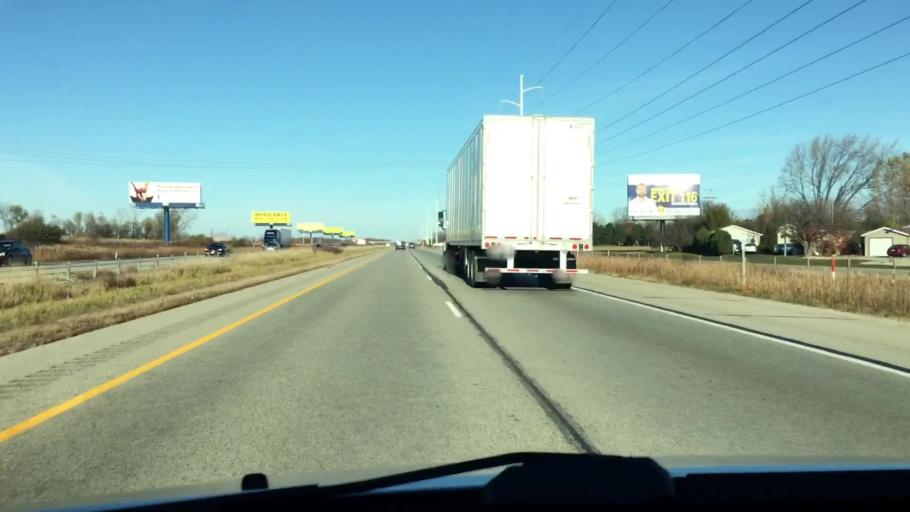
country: US
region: Wisconsin
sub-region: Fond du Lac County
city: North Fond du Lac
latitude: 43.8149
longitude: -88.5131
